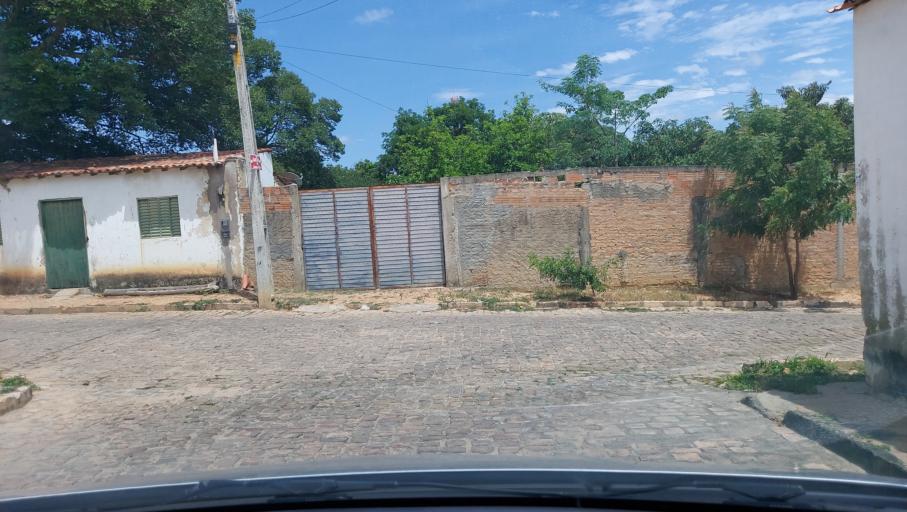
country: BR
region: Bahia
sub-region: Oliveira Dos Brejinhos
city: Beira Rio
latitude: -11.9968
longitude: -42.6296
